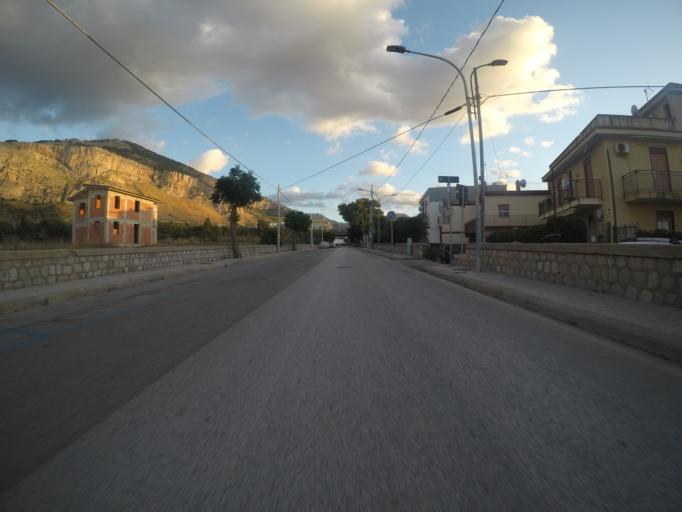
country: IT
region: Sicily
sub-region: Palermo
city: Isola delle Femmine
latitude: 38.1831
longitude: 13.2380
